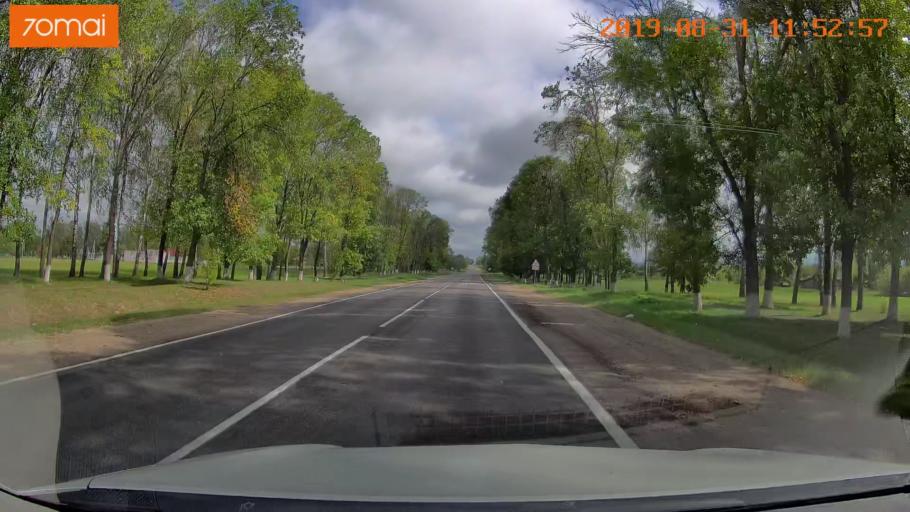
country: BY
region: Mogilev
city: Cherykaw
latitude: 53.6256
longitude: 31.5337
